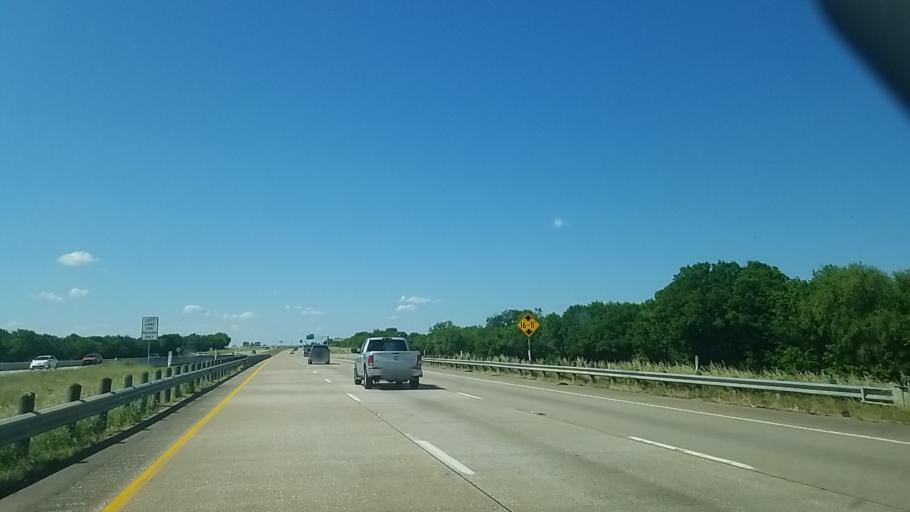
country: US
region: Texas
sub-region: Ellis County
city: Ferris
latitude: 32.5044
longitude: -96.6636
